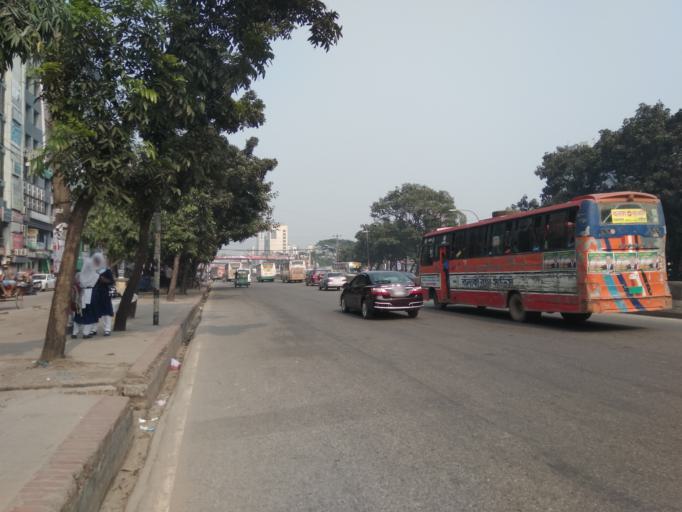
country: BD
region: Dhaka
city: Tungi
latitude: 23.8668
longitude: 90.4001
